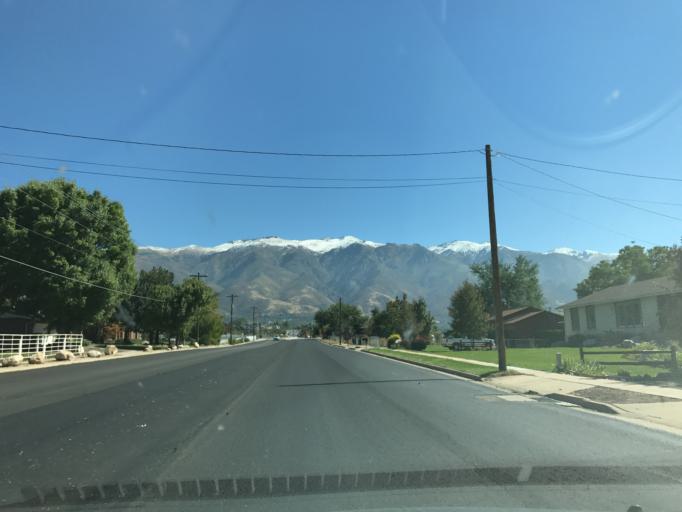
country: US
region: Utah
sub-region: Davis County
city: Hill Air Force Bace
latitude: 41.0888
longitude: -111.9481
